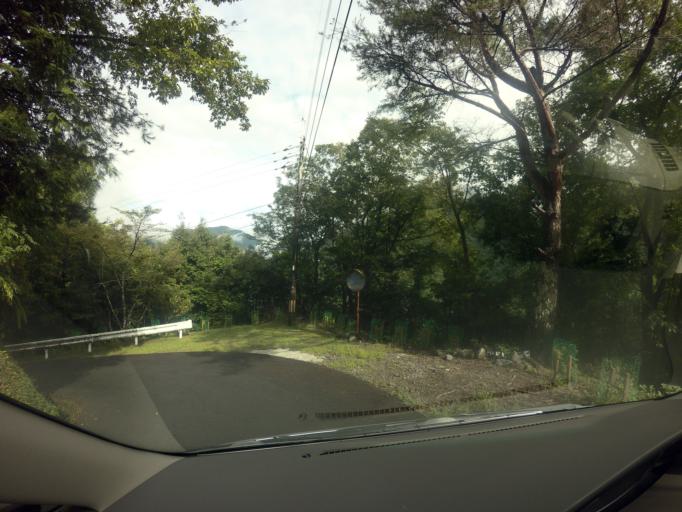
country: JP
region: Wakayama
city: Shingu
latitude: 33.9687
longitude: 135.8110
